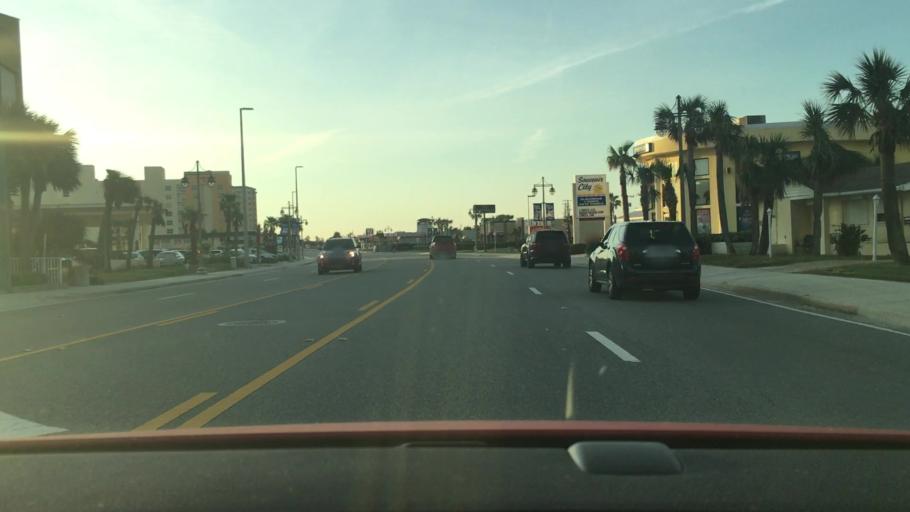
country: US
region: Florida
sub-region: Volusia County
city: Daytona Beach Shores
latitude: 29.1620
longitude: -80.9751
